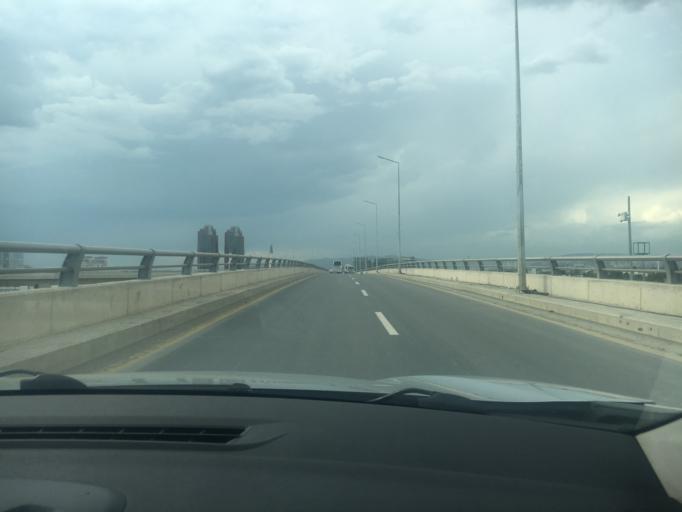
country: TR
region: Ankara
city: Batikent
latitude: 39.8990
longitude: 32.7669
